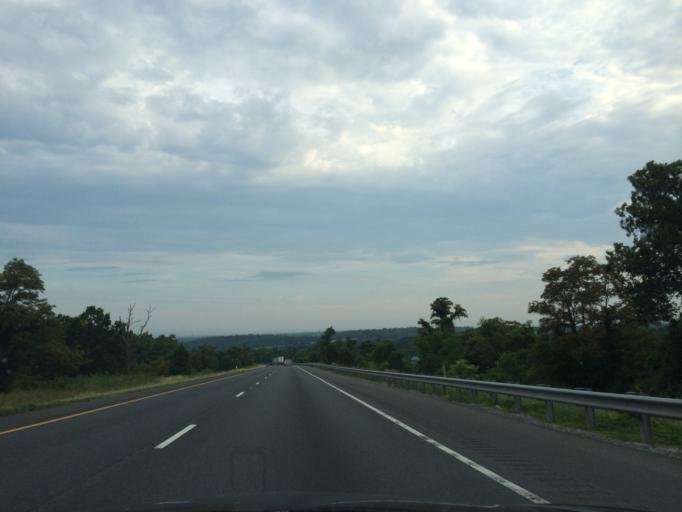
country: US
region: Maryland
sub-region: Washington County
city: Boonsboro
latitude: 39.5649
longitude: -77.6166
